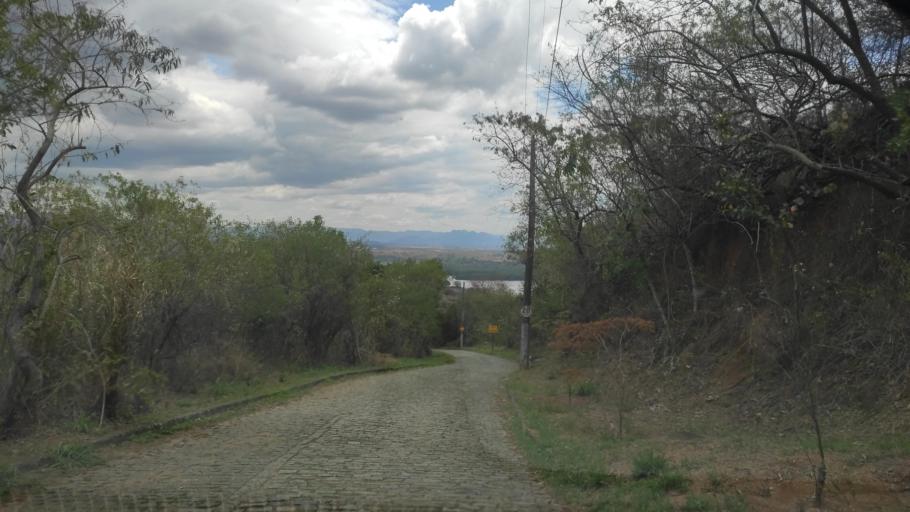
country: BR
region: Espirito Santo
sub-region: Vitoria
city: Vitoria
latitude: -20.2938
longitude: -40.3373
